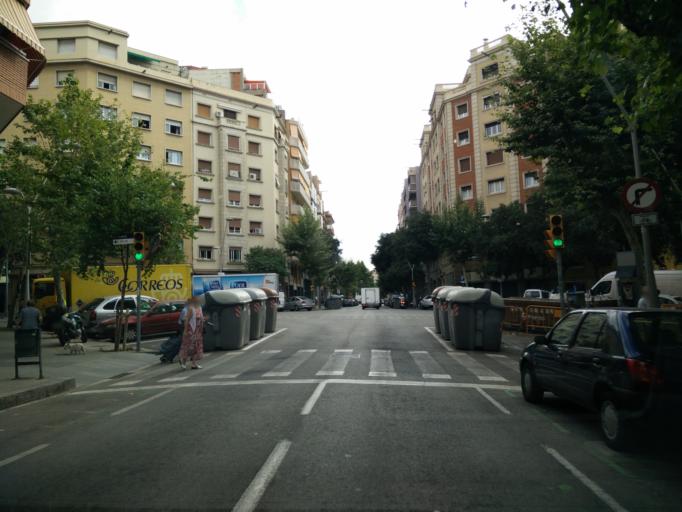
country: ES
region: Catalonia
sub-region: Provincia de Barcelona
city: Barcelona
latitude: 41.3854
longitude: 2.1469
